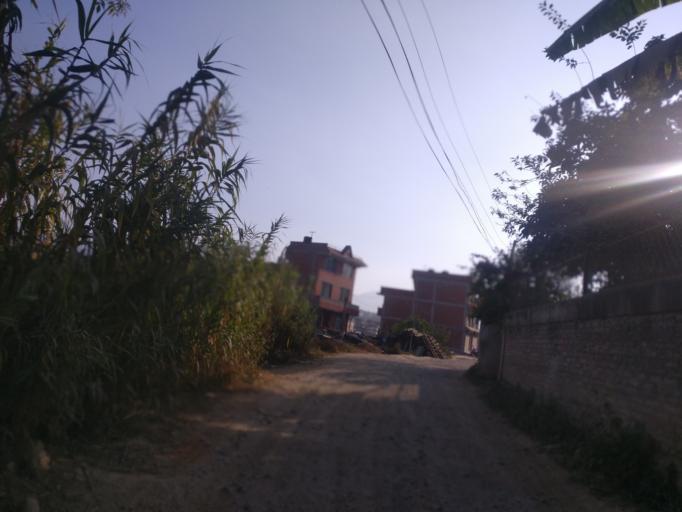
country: NP
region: Central Region
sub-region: Bagmati Zone
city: Patan
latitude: 27.6545
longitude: 85.3328
